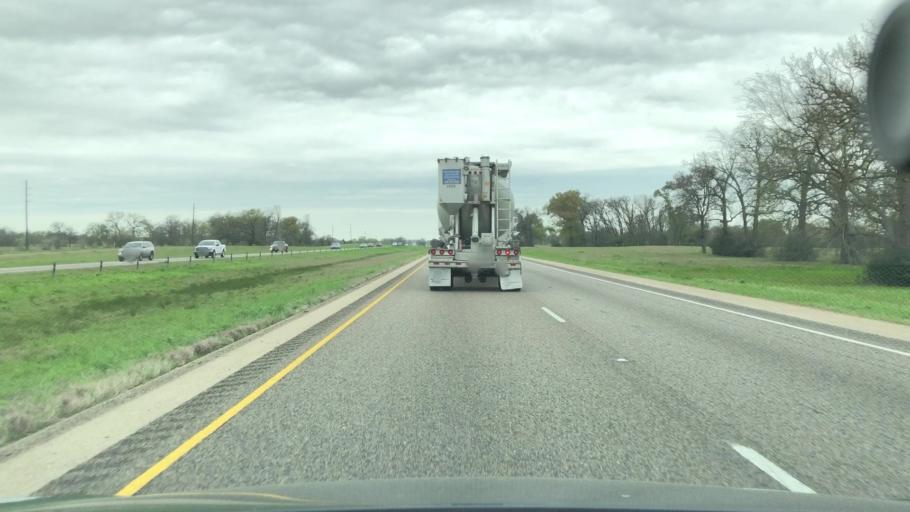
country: US
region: Texas
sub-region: Madison County
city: Madisonville
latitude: 31.0536
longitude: -95.9476
